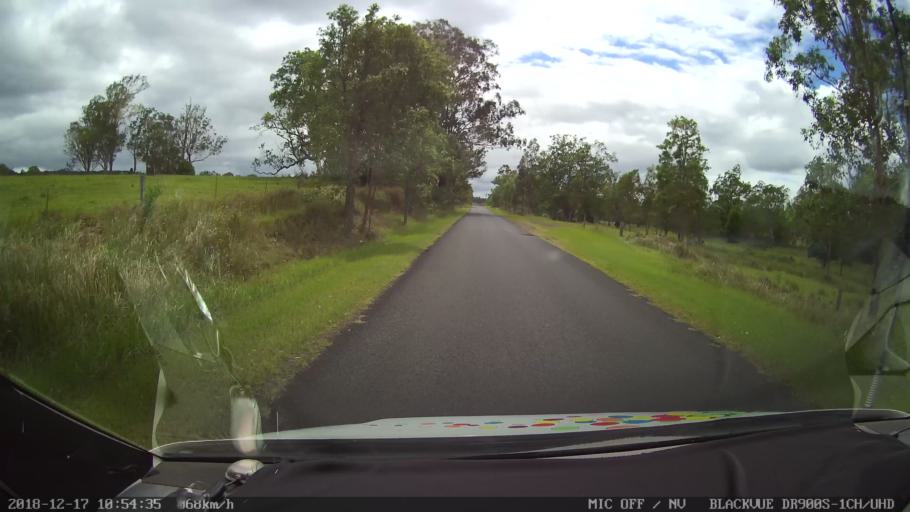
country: AU
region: New South Wales
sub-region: Tenterfield Municipality
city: Carrolls Creek
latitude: -28.8286
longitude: 152.5689
